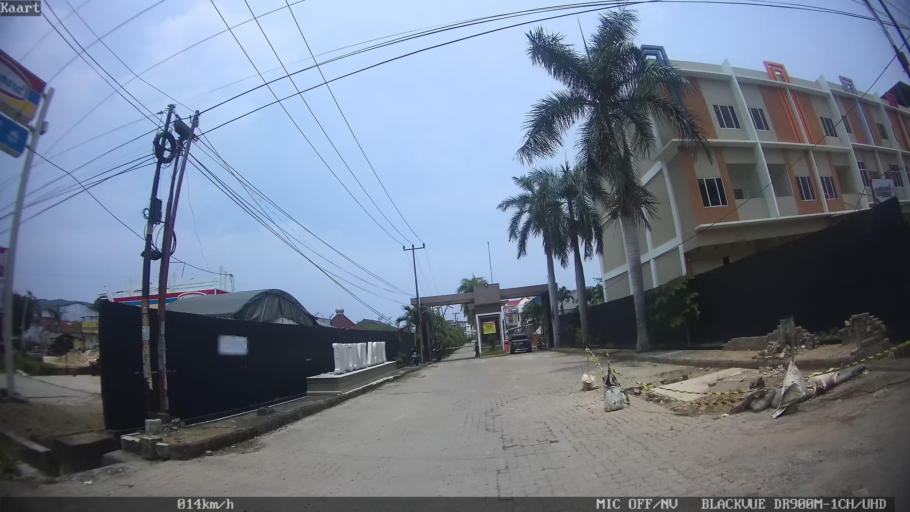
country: ID
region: Lampung
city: Bandarlampung
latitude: -5.4115
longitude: 105.2889
